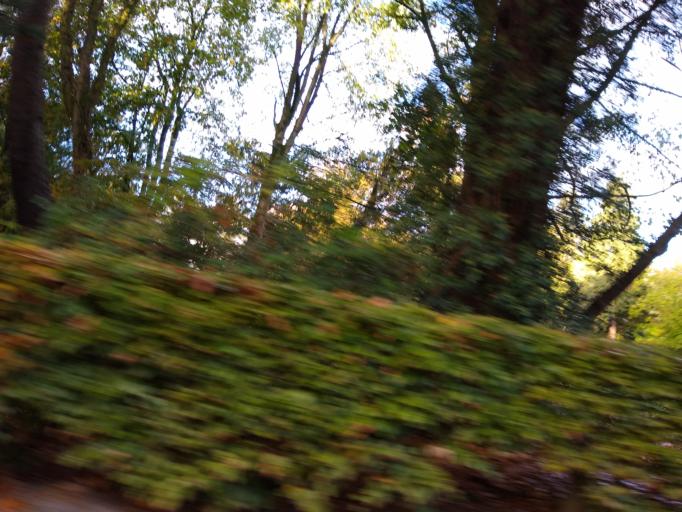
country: DE
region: Lower Saxony
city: Rastede
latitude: 53.2414
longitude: 8.1992
